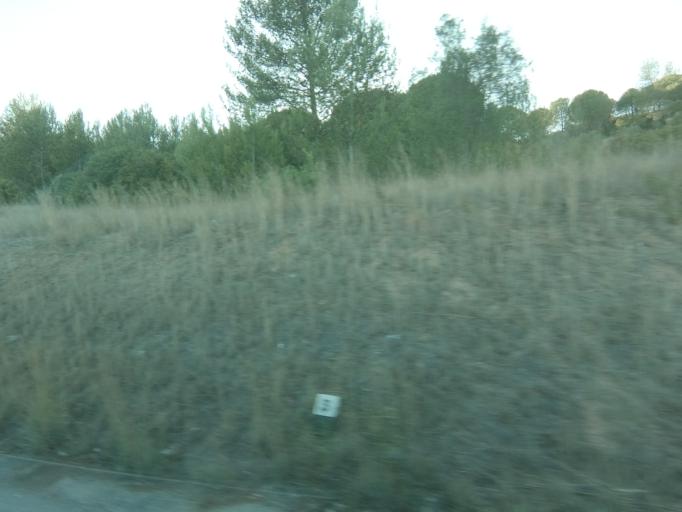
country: PT
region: Setubal
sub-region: Palmela
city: Quinta do Anjo
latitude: 38.5237
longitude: -8.9831
